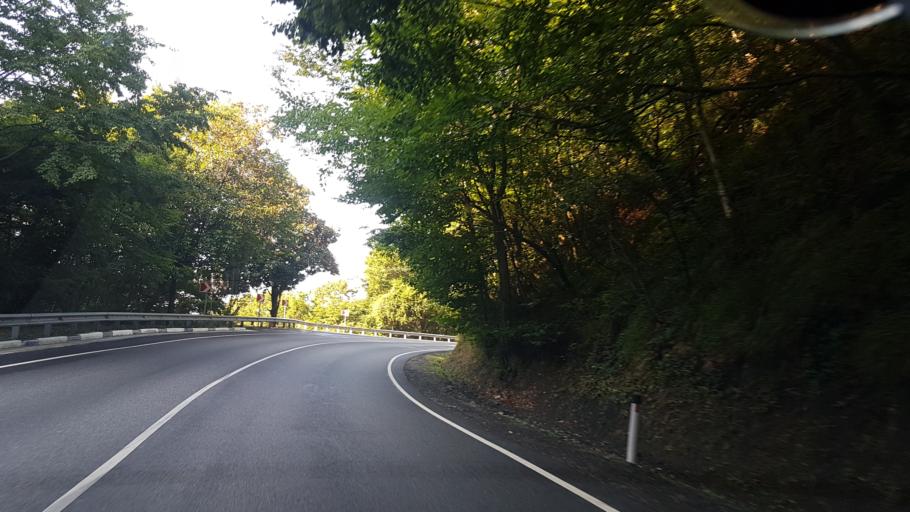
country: RU
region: Krasnodarskiy
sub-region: Sochi City
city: Lazarevskoye
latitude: 43.8265
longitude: 39.4344
